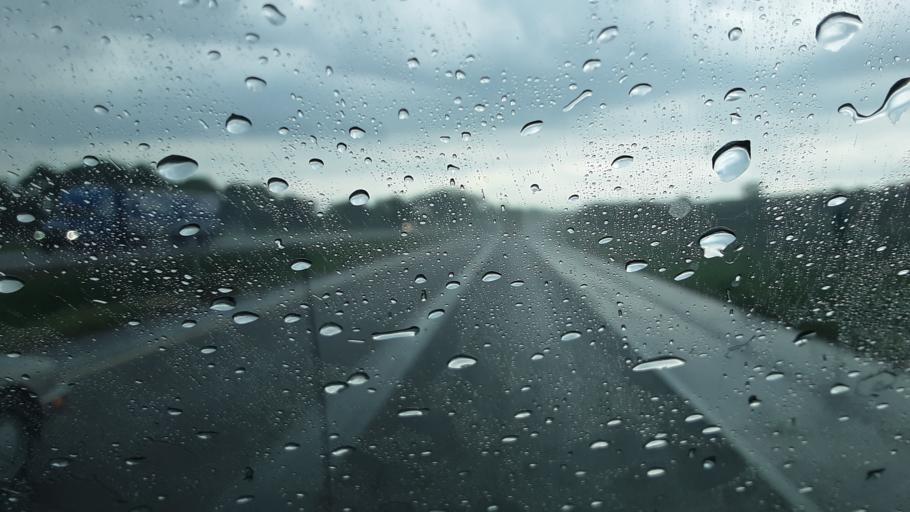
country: US
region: Iowa
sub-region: Pottawattamie County
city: Council Bluffs
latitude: 41.3114
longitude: -95.7621
